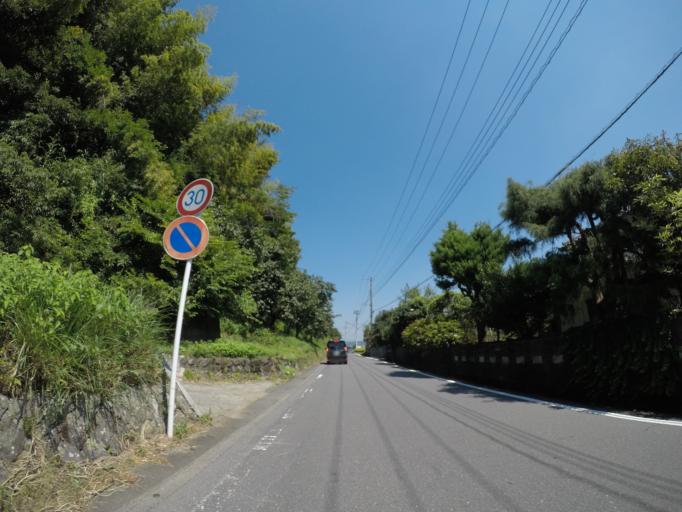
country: JP
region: Shizuoka
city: Fujinomiya
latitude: 35.2106
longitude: 138.5647
